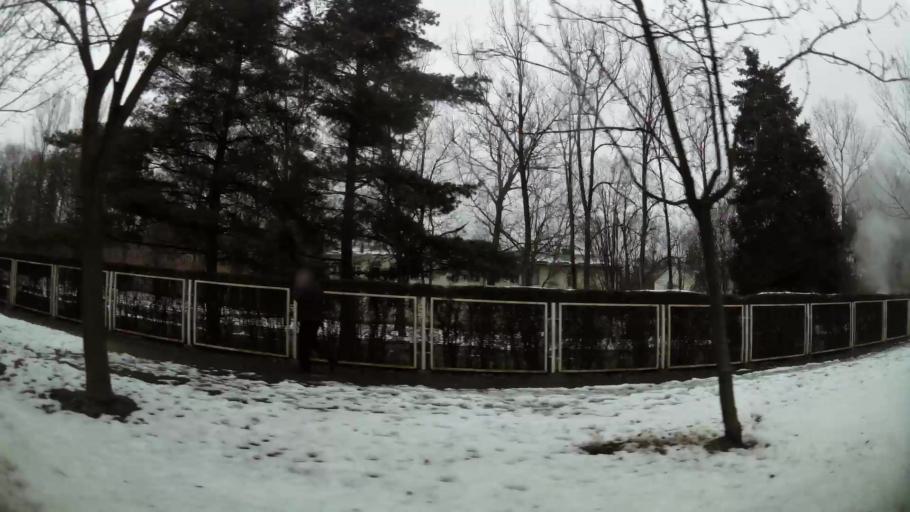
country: RS
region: Central Serbia
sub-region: Belgrade
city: Vozdovac
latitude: 44.7645
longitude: 20.4646
